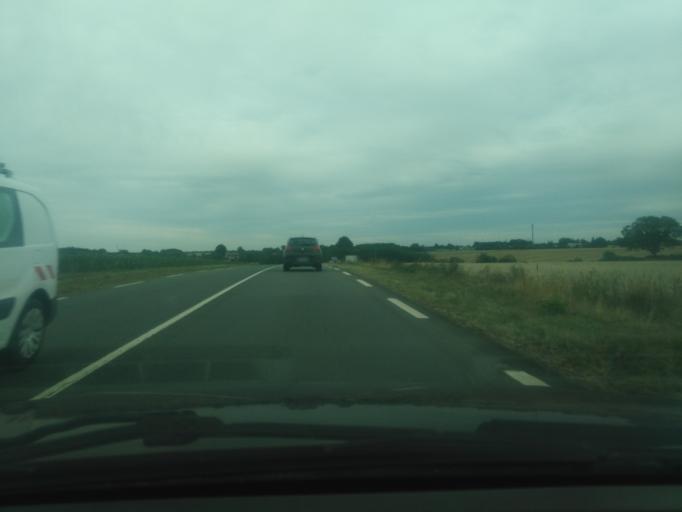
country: FR
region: Poitou-Charentes
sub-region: Departement de la Vienne
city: Saint-Savin
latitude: 46.5688
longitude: 0.8430
